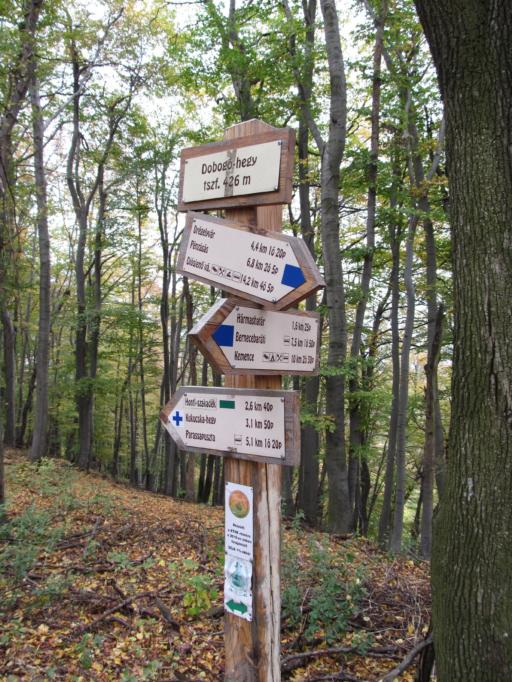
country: SK
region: Nitriansky
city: Sahy
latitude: 48.0270
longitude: 18.9958
